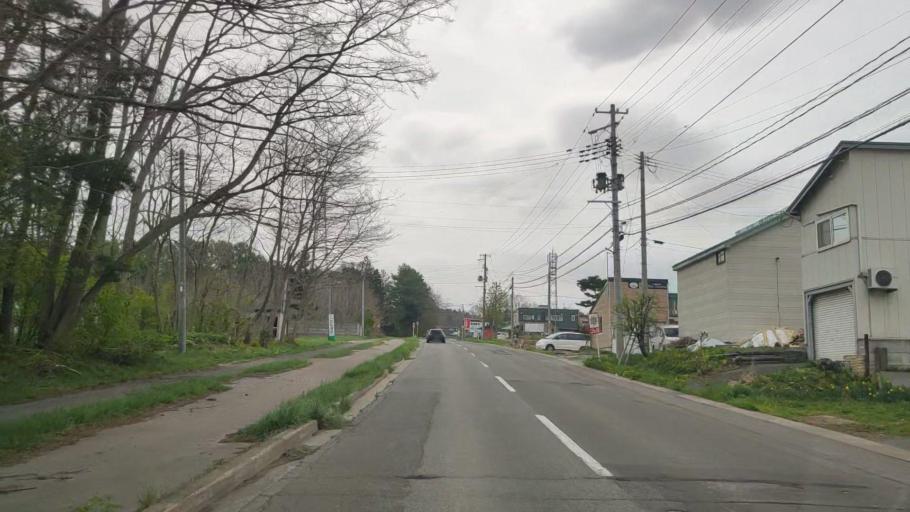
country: JP
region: Aomori
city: Aomori Shi
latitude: 40.7697
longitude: 140.7993
